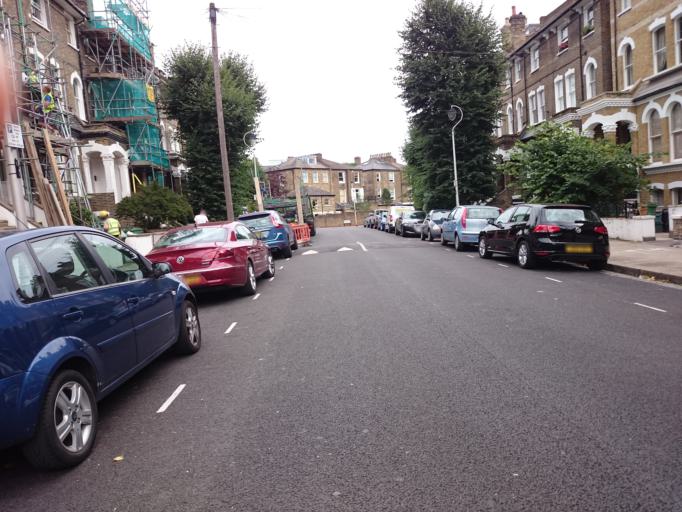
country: GB
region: England
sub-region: Greater London
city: Holloway
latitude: 51.5538
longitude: -0.1365
